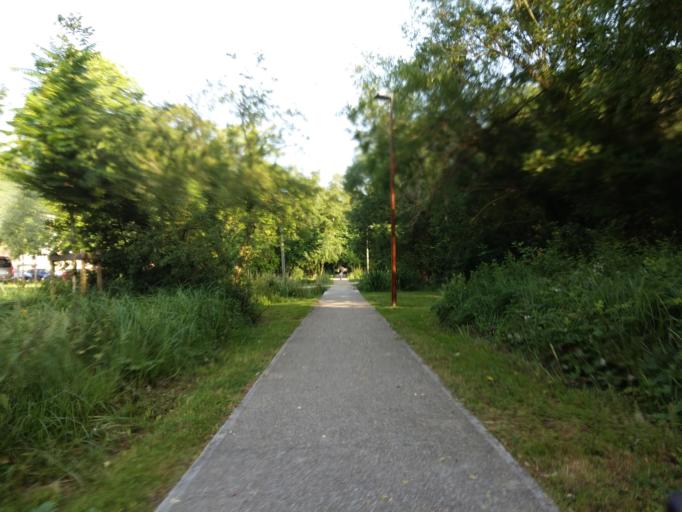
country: FR
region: Picardie
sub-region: Departement de la Somme
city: Amiens
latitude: 49.9007
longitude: 2.2924
